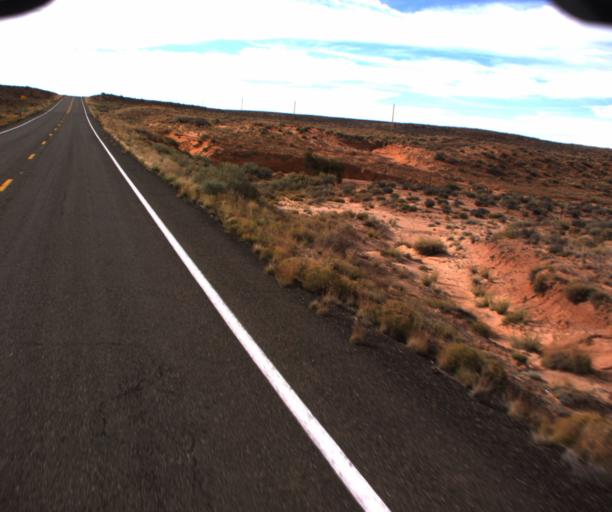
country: US
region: Arizona
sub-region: Coconino County
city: LeChee
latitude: 36.7632
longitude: -111.2852
